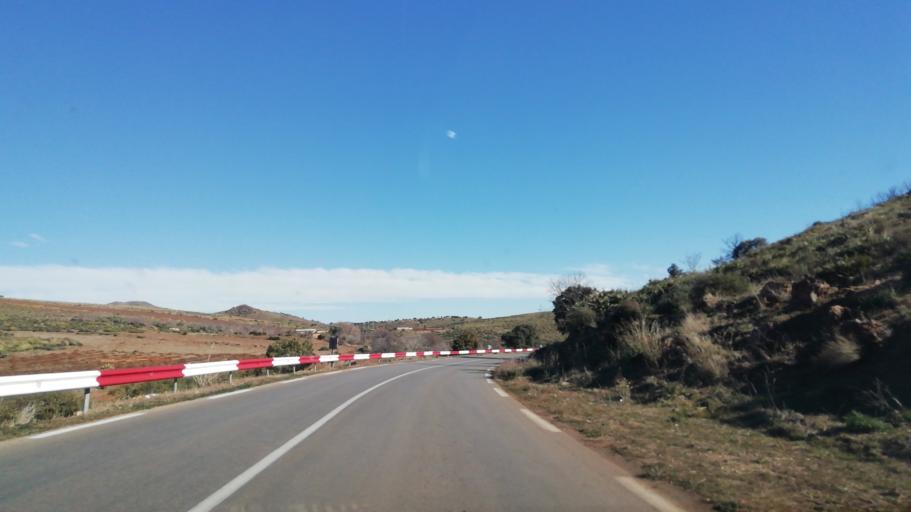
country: DZ
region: Tlemcen
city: Ouled Mimoun
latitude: 34.7720
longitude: -1.1358
